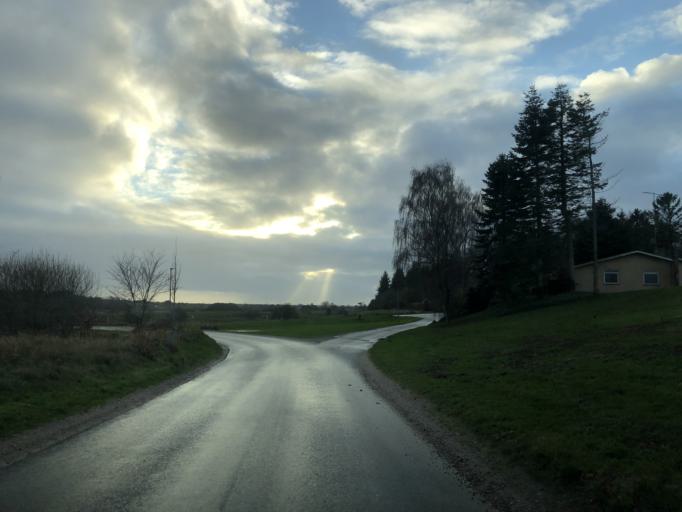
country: DK
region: Central Jutland
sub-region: Viborg Kommune
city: Viborg
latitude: 56.4770
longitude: 9.3411
